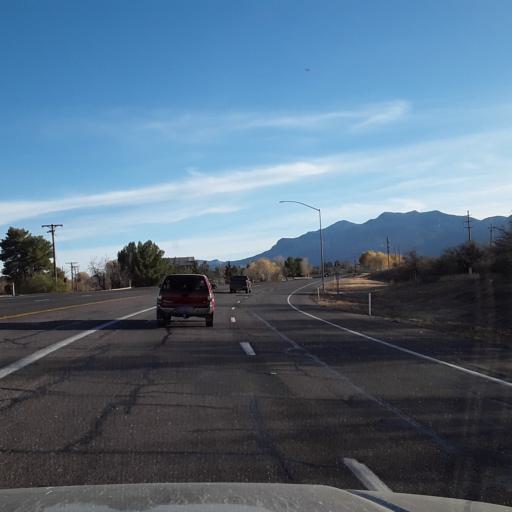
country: US
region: Arizona
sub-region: Cochise County
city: Sierra Vista
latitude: 31.5612
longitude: -110.3090
